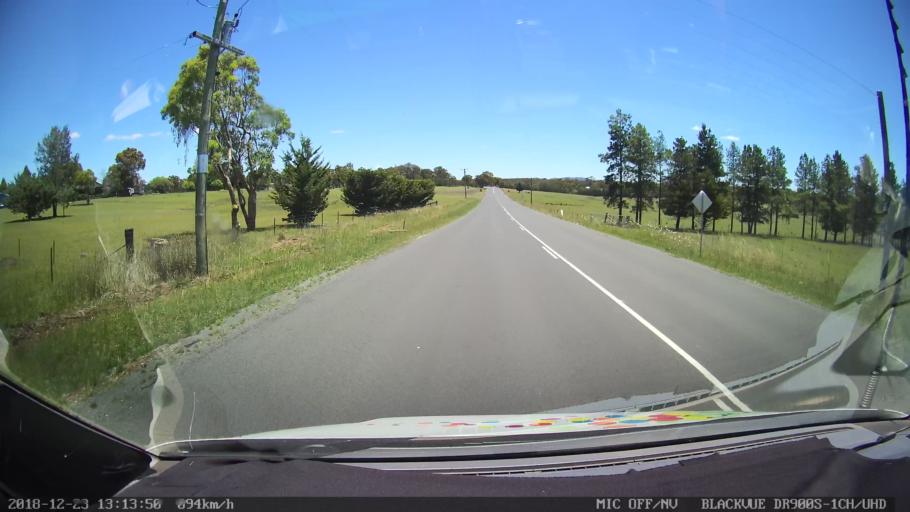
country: AU
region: New South Wales
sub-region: Armidale Dumaresq
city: Armidale
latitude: -30.5031
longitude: 151.5359
